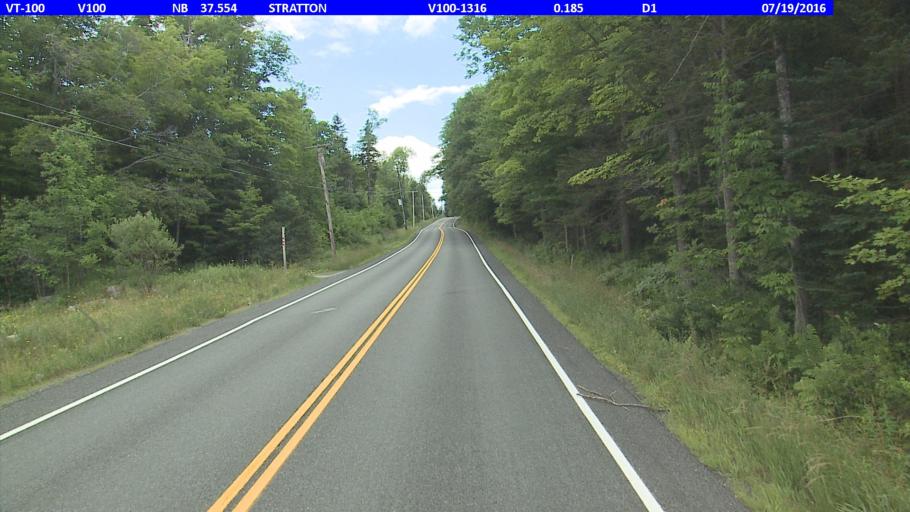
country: US
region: Vermont
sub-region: Windham County
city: Dover
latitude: 42.9940
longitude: -72.8882
